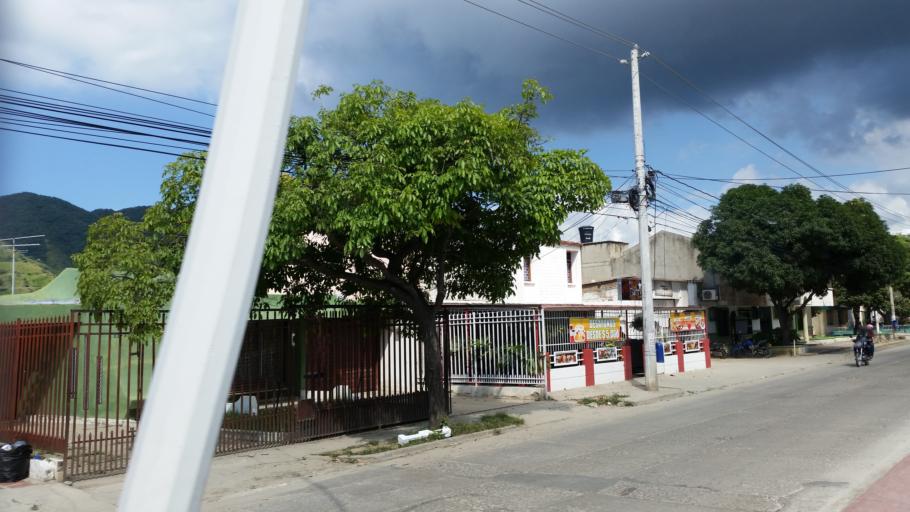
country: CO
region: Magdalena
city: Santa Marta
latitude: 11.2411
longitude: -74.1884
